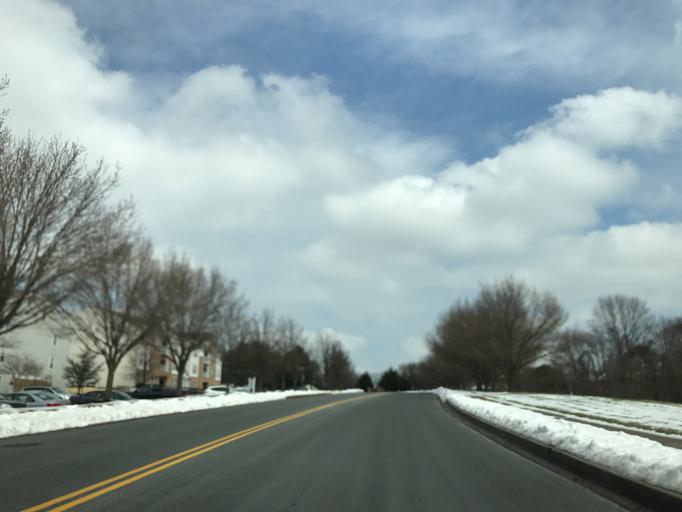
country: US
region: Maryland
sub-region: Harford County
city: Bel Air North
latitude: 39.5625
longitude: -76.3778
